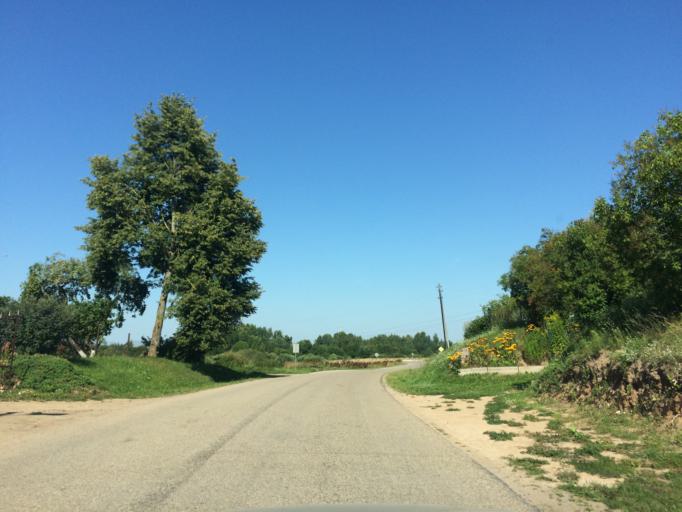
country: LV
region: Rezekne
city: Rezekne
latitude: 56.5089
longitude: 27.3120
